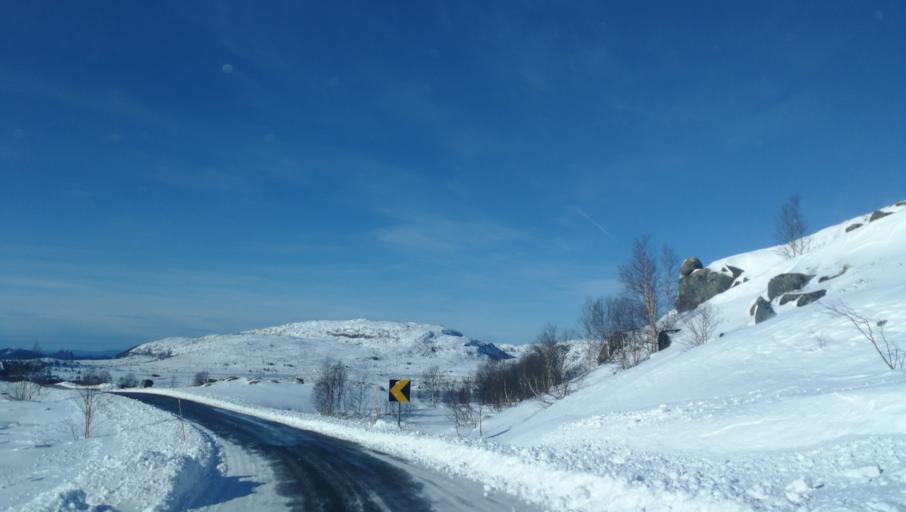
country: NO
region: Rogaland
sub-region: Hjelmeland
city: Hjelmelandsvagen
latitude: 59.1091
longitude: 6.3721
